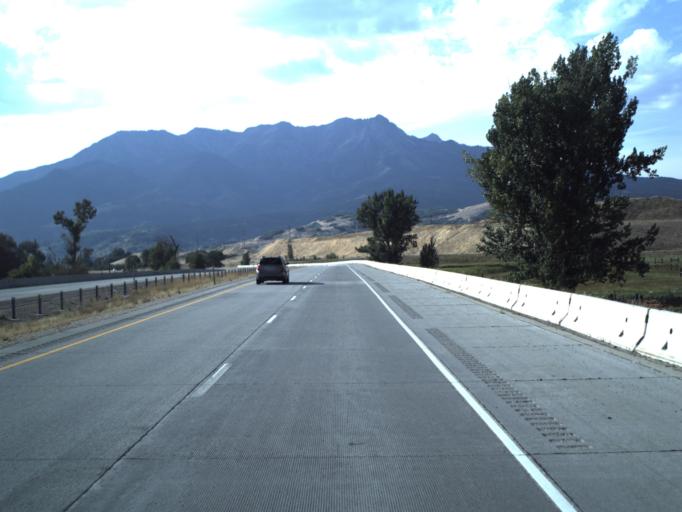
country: US
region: Utah
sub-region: Morgan County
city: Mountain Green
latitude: 41.1349
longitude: -111.7840
